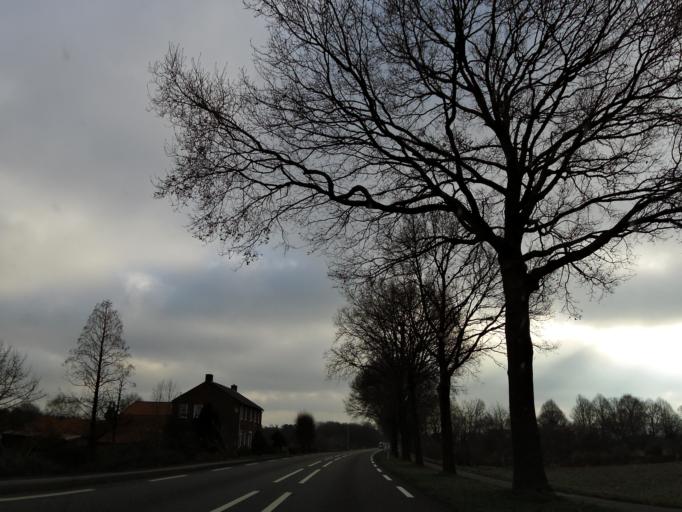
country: NL
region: North Brabant
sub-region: Gemeente Boxmeer
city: Boxmeer
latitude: 51.6202
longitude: 6.0305
